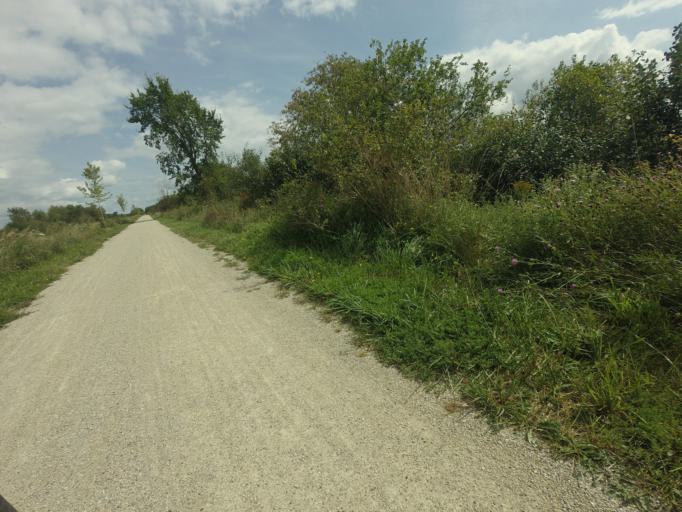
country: CA
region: Ontario
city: North Perth
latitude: 43.5746
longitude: -80.8296
